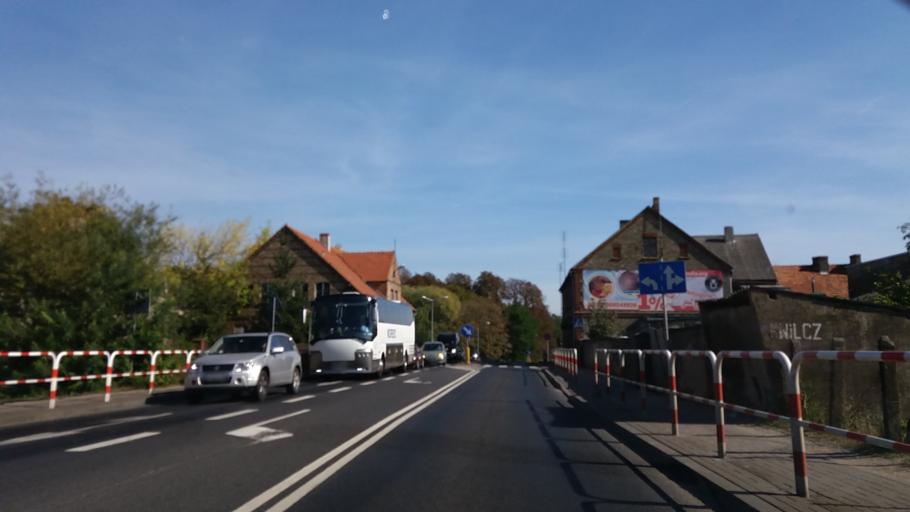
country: PL
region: Greater Poland Voivodeship
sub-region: Powiat miedzychodzki
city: Kwilcz
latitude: 52.5550
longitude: 16.0843
